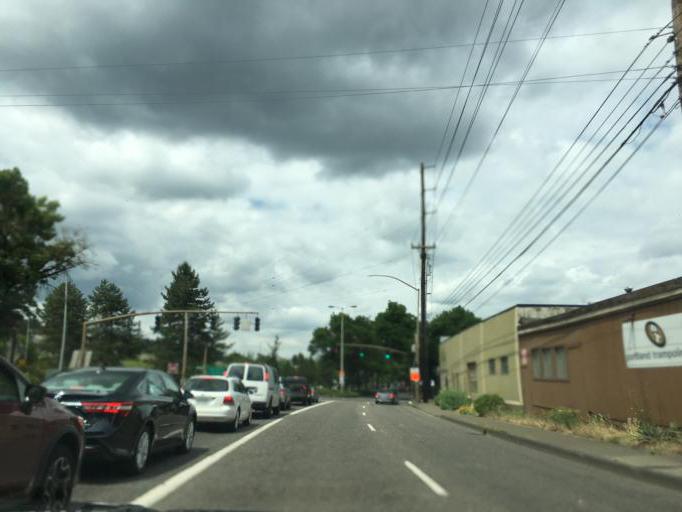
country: US
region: Oregon
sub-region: Clackamas County
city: Milwaukie
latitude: 45.4707
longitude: -122.6716
